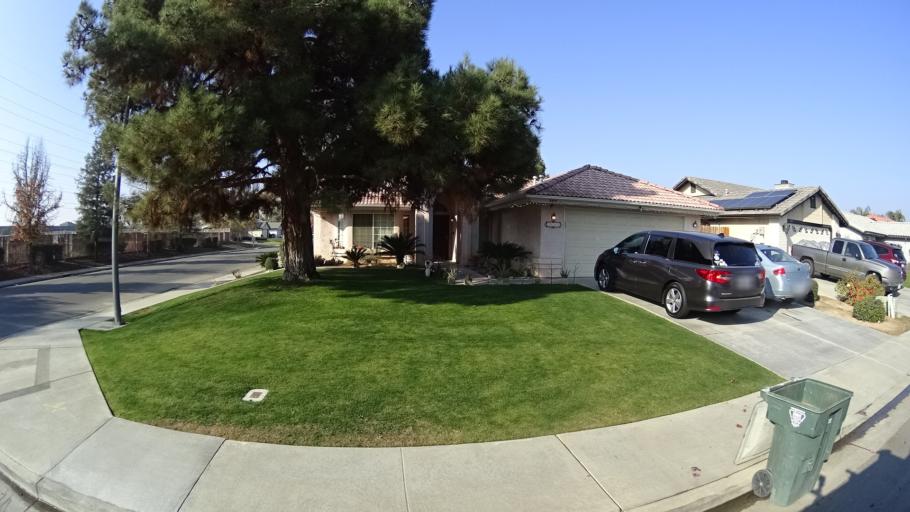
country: US
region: California
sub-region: Kern County
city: Greenacres
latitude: 35.3877
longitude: -119.1066
